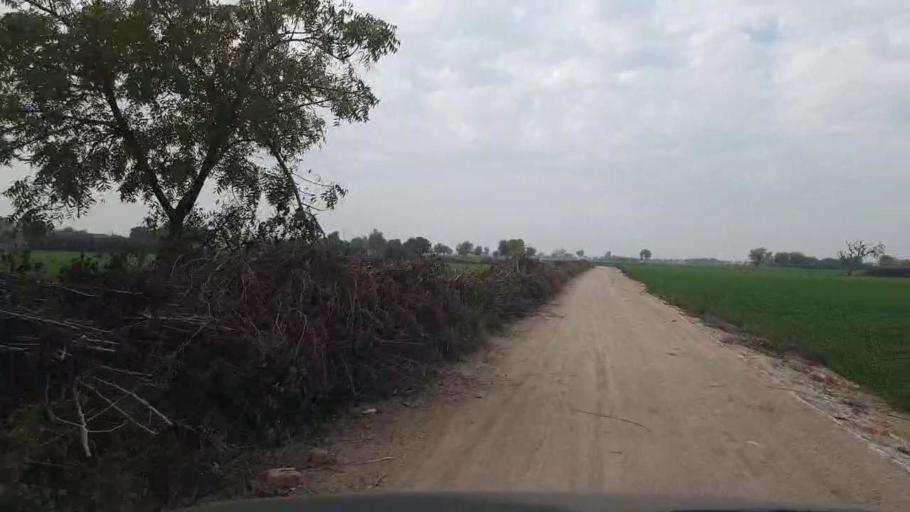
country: PK
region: Sindh
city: Sakrand
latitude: 26.0369
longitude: 68.3992
